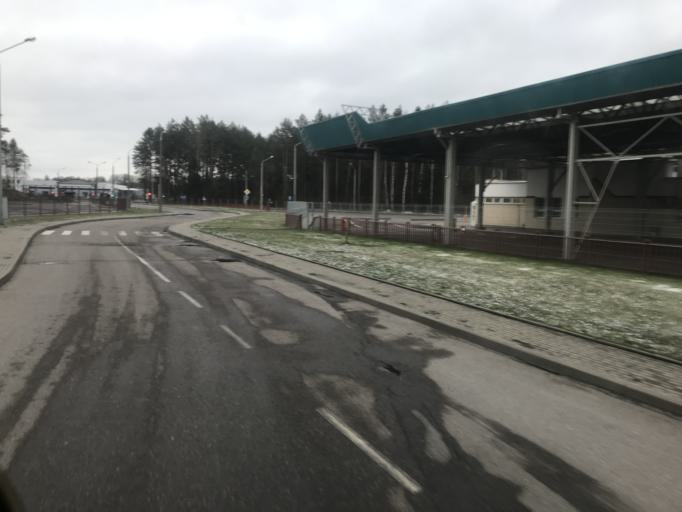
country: BY
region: Grodnenskaya
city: Vyalikaya Byerastavitsa
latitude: 53.1212
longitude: 23.8975
